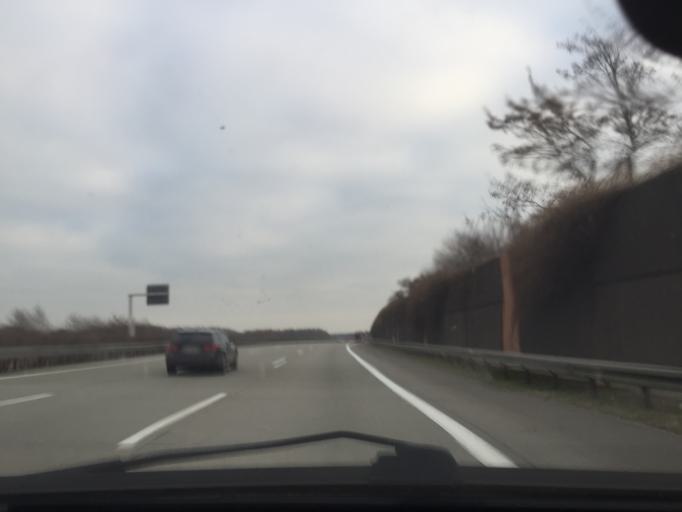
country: DE
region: Brandenburg
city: Gross Kreutz
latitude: 52.3401
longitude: 12.7170
